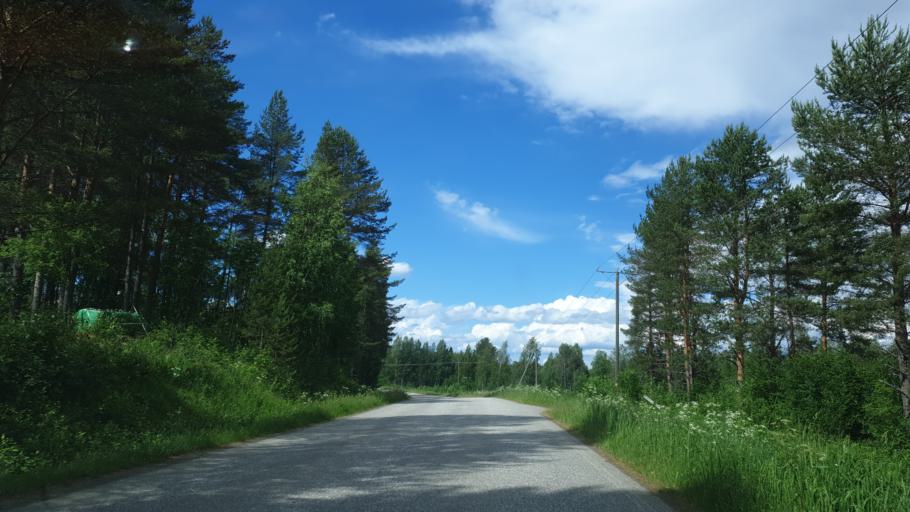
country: FI
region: Northern Savo
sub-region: Koillis-Savo
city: Kaavi
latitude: 62.9976
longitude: 28.7163
